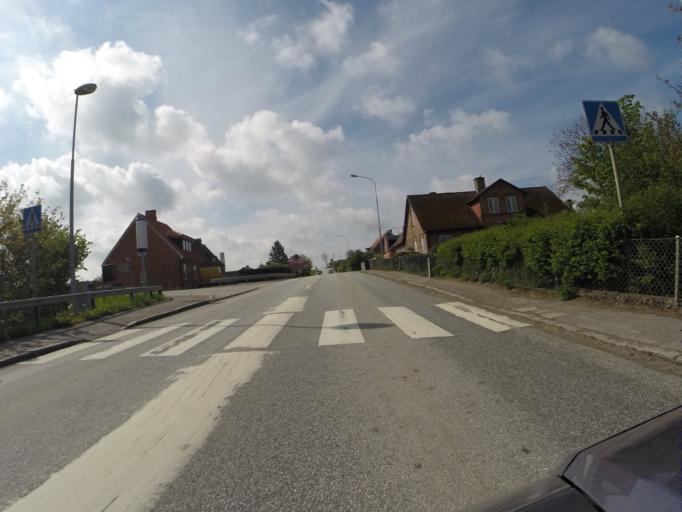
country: SE
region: Skane
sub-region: Landskrona
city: Asmundtorp
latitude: 55.9243
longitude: 12.9553
